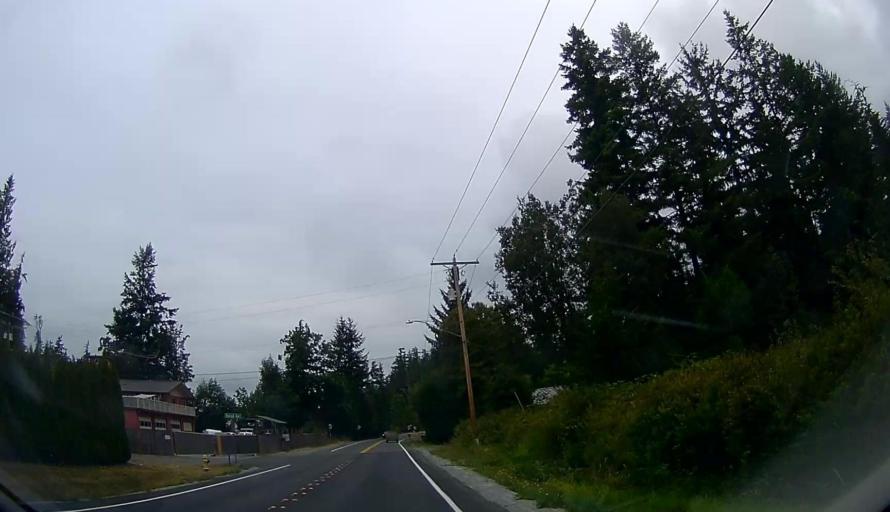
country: US
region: Washington
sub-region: Snohomish County
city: Warm Beach
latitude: 48.1674
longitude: -122.3575
